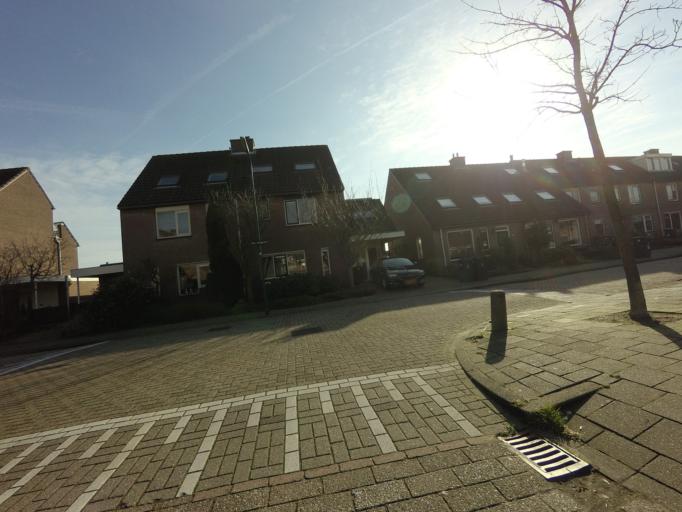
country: NL
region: Utrecht
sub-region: Gemeente Montfoort
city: Montfoort
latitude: 52.0654
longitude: 4.9183
